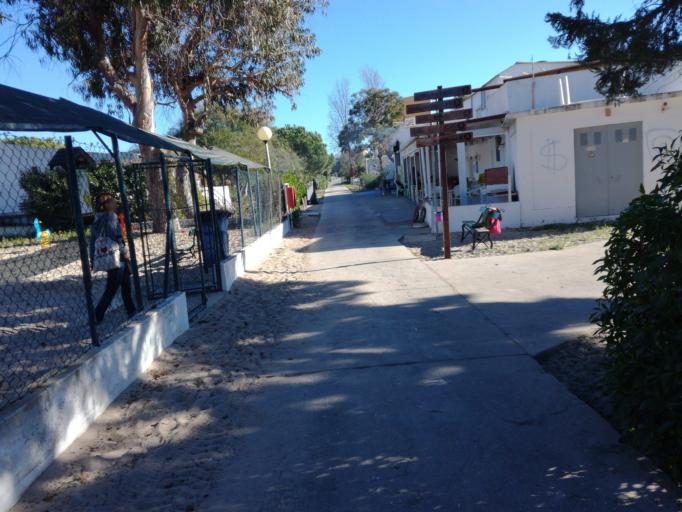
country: PT
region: Faro
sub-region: Olhao
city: Olhao
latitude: 37.0193
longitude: -7.8030
